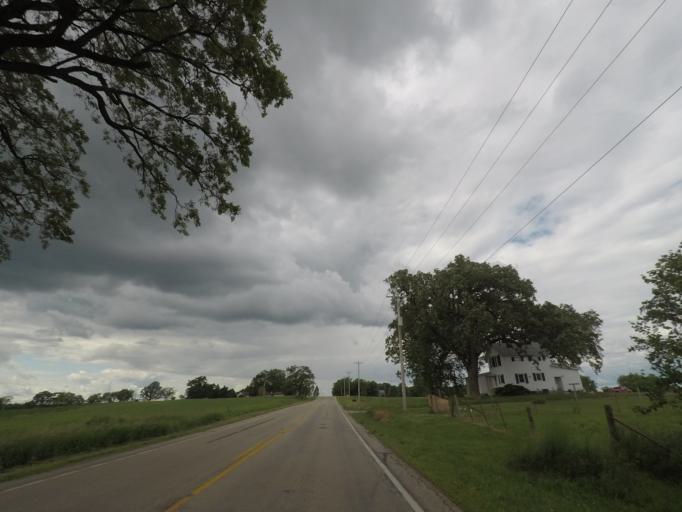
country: US
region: Wisconsin
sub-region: Green County
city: Brooklyn
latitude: 42.8408
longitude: -89.4125
